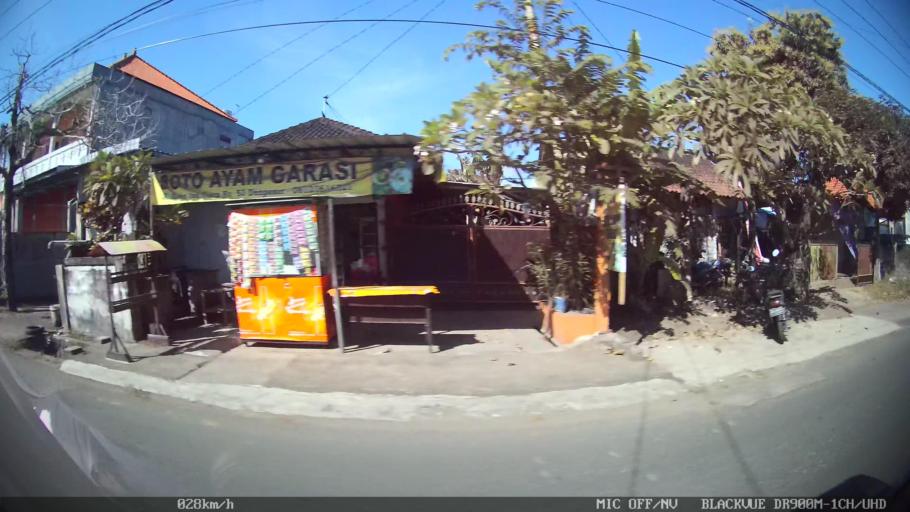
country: ID
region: Bali
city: Banjar Kertasari
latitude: -8.6240
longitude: 115.1856
